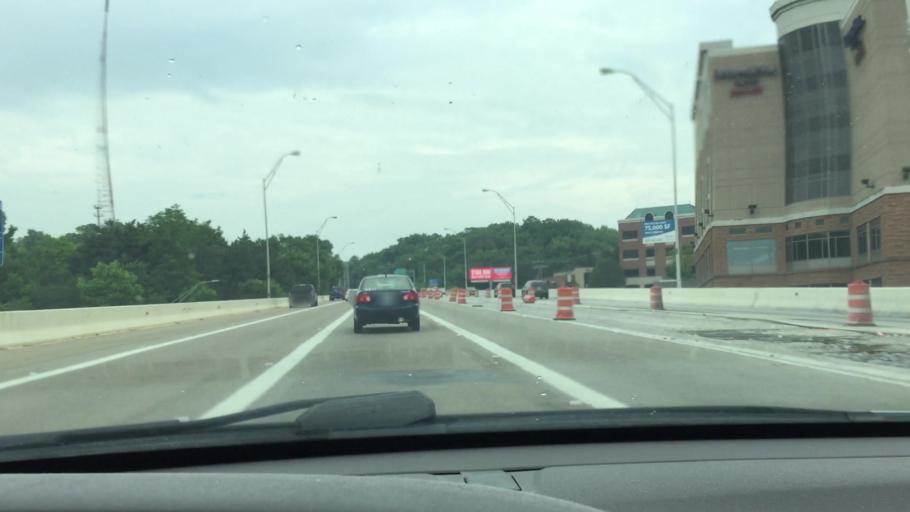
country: US
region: Kentucky
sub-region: Campbell County
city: Bellevue
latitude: 39.1177
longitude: -84.4993
